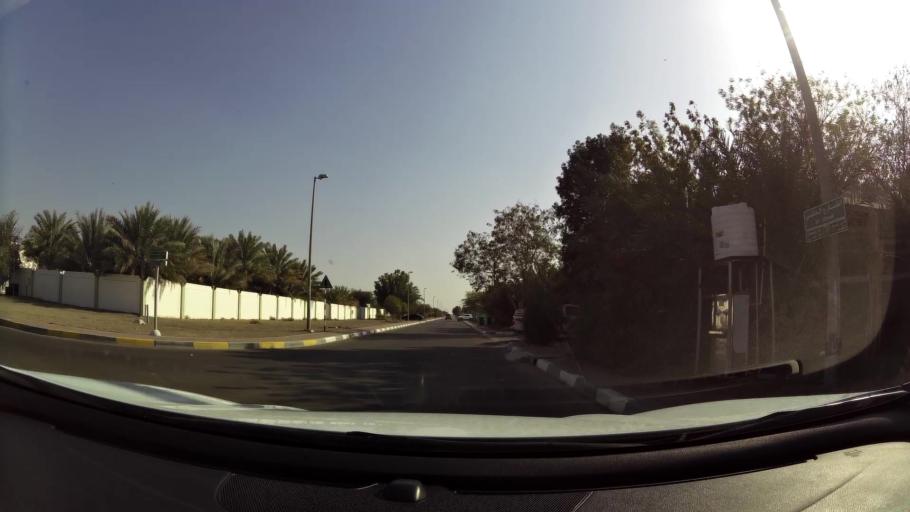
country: AE
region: Abu Dhabi
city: Al Ain
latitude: 24.0769
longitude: 55.8630
